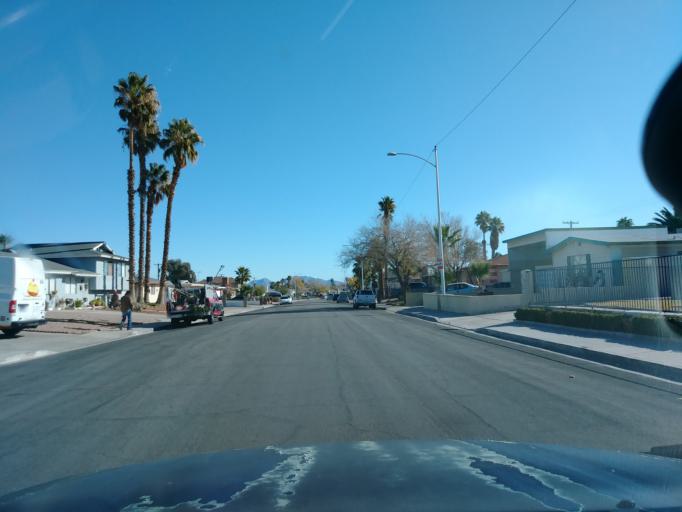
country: US
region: Nevada
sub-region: Clark County
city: Spring Valley
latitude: 36.1765
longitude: -115.2318
